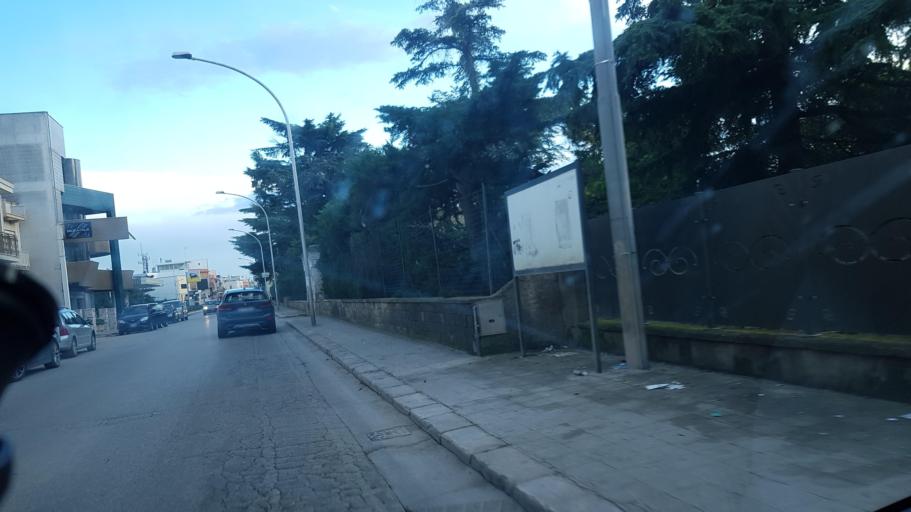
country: IT
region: Apulia
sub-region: Provincia di Brindisi
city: San Vito dei Normanni
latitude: 40.6607
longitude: 17.7041
